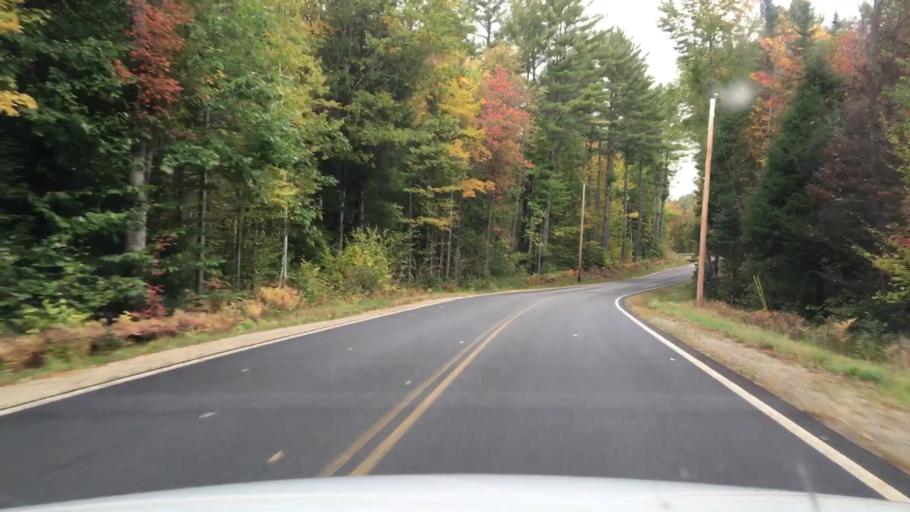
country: US
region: Maine
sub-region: Oxford County
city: Bethel
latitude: 44.2737
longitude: -70.7304
